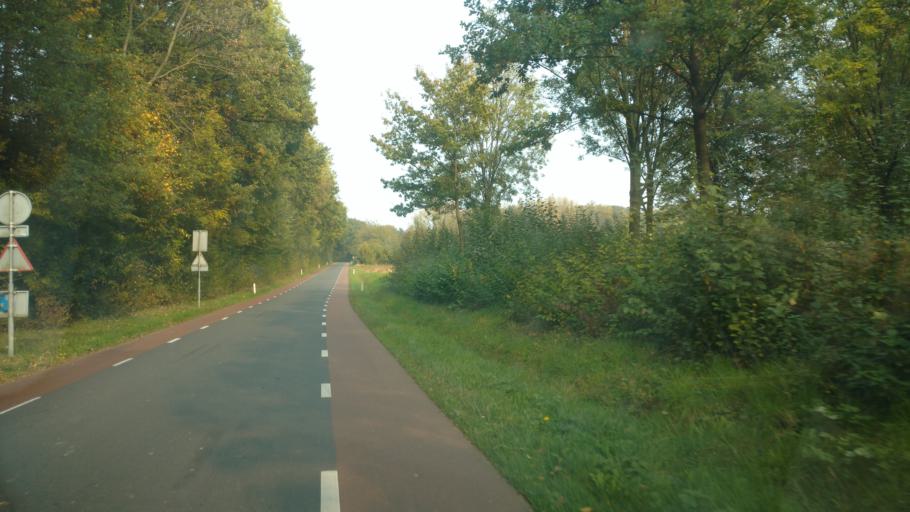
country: NL
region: Limburg
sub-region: Gemeente Meerssen
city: Meerssen
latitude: 50.8933
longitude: 5.7472
